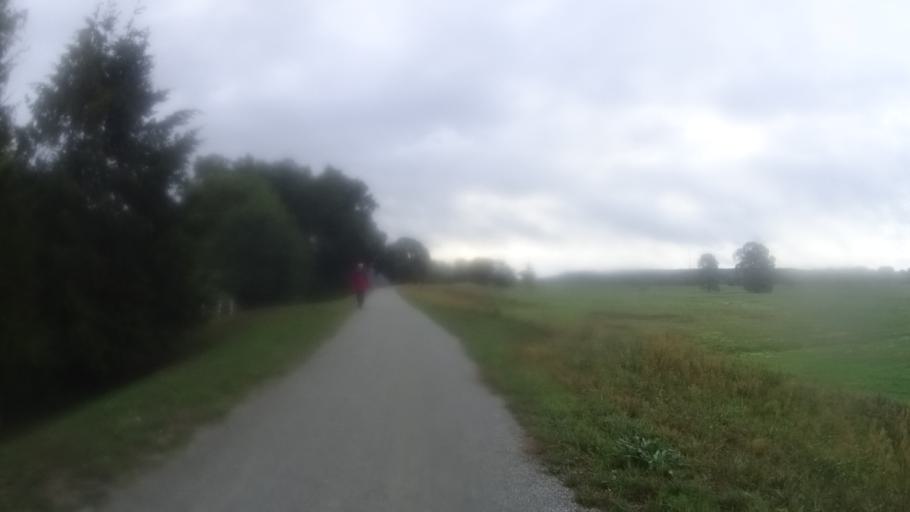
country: DE
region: Lower Saxony
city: Gorleben
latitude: 53.0769
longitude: 11.3939
